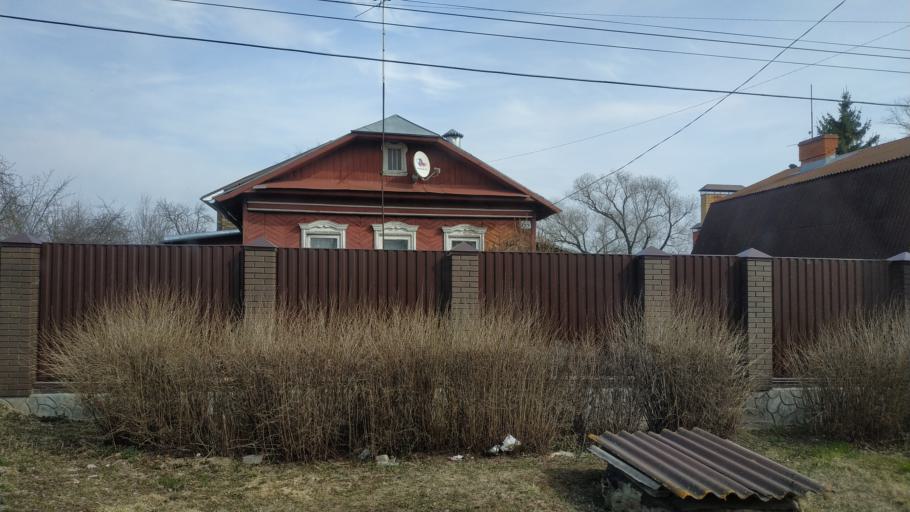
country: RU
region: Moskovskaya
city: Voskresensk
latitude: 55.3401
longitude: 38.6216
